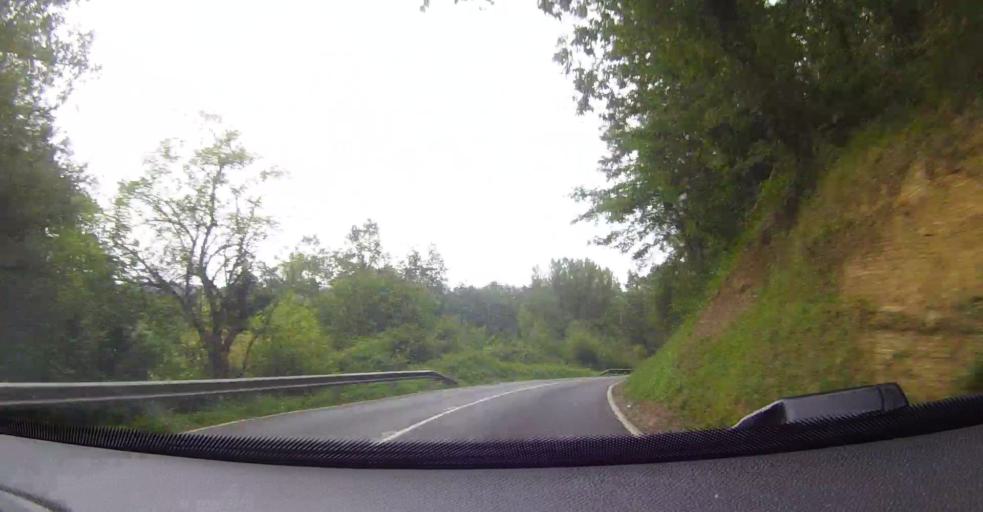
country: ES
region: Basque Country
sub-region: Bizkaia
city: Balmaseda
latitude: 43.2405
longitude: -3.2290
